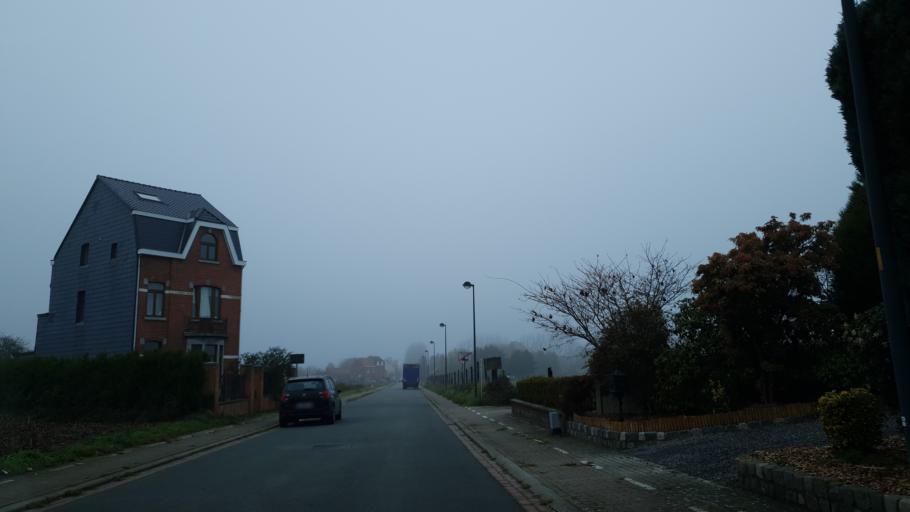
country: BE
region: Flanders
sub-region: Provincie Vlaams-Brabant
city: Kortenberg
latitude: 50.8751
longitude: 4.5178
